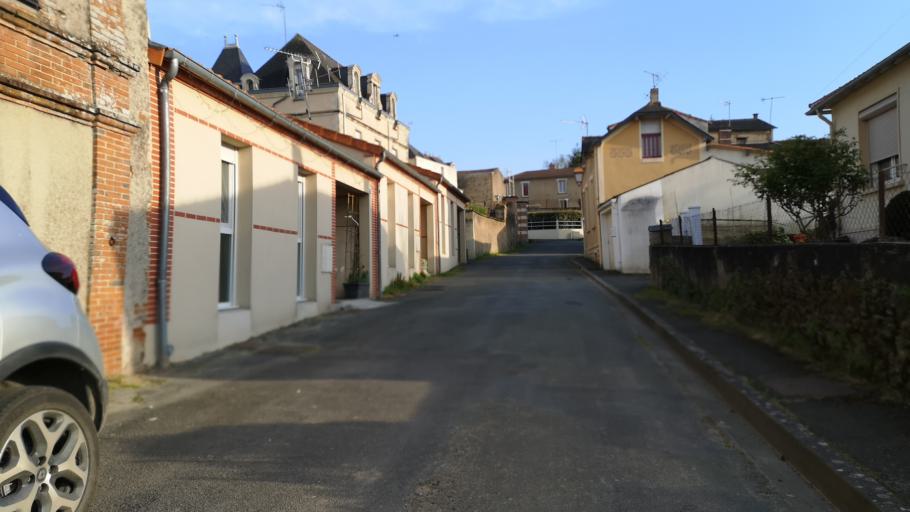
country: FR
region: Pays de la Loire
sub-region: Departement de Maine-et-Loire
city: Chemille-Melay
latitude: 47.2068
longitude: -0.7277
